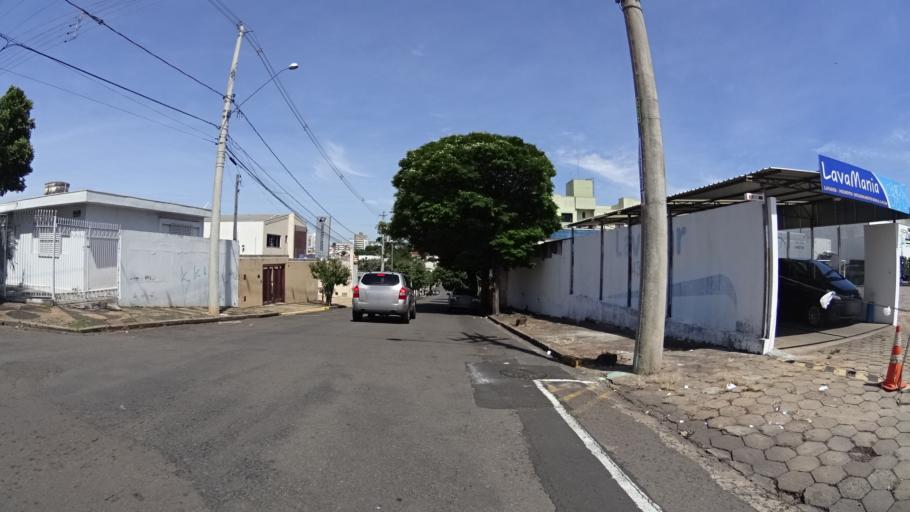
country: BR
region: Sao Paulo
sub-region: Marilia
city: Marilia
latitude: -22.2242
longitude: -49.9363
